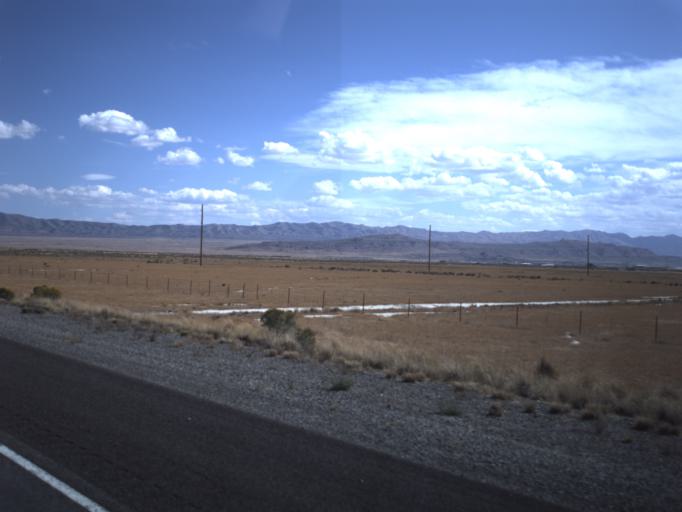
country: US
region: Utah
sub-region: Tooele County
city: Grantsville
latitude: 40.7251
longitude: -113.1459
